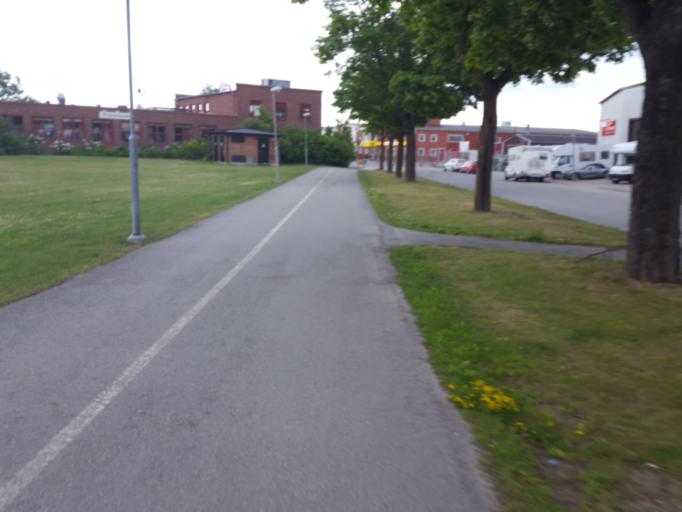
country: SE
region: Uppsala
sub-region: Uppsala Kommun
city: Uppsala
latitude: 59.8542
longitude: 17.6598
